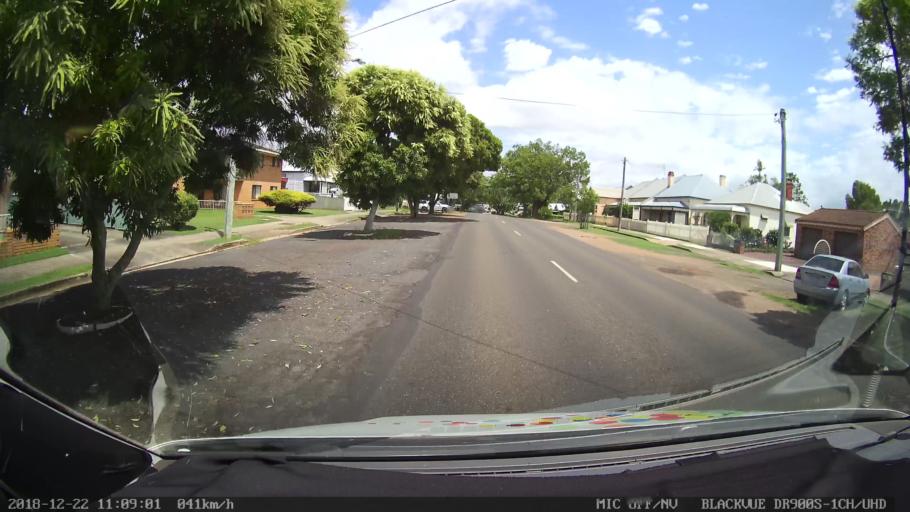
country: AU
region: New South Wales
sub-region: Clarence Valley
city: Grafton
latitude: -29.6874
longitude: 152.9313
